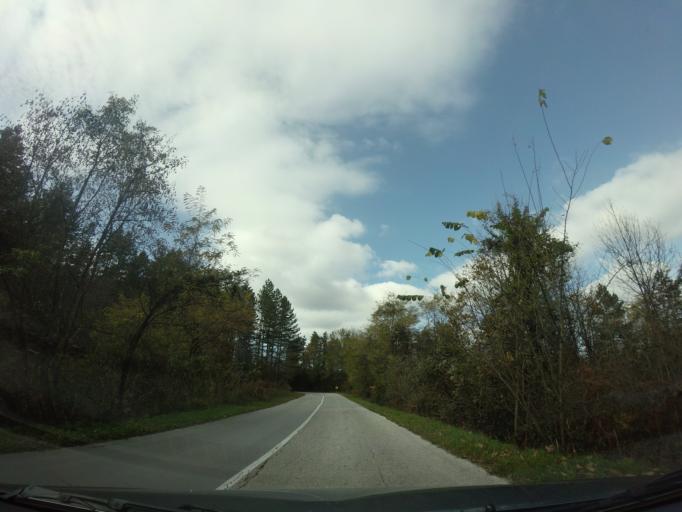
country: HR
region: Karlovacka
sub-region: Grad Karlovac
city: Slunj
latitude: 45.1434
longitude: 15.5199
